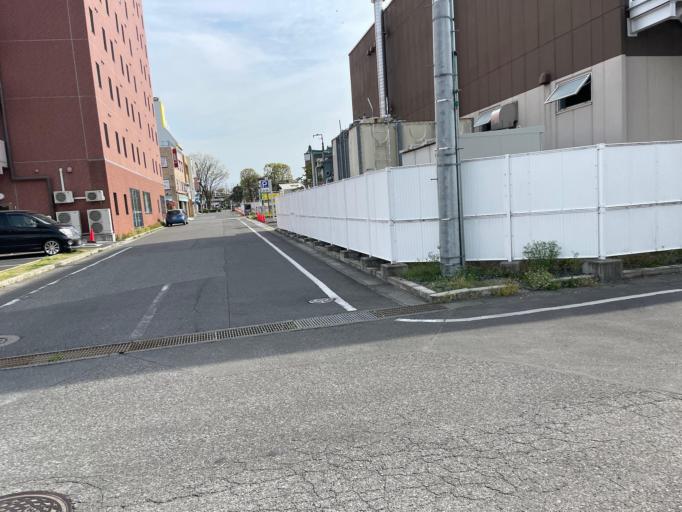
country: JP
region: Saitama
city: Fukayacho
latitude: 36.1933
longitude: 139.2816
